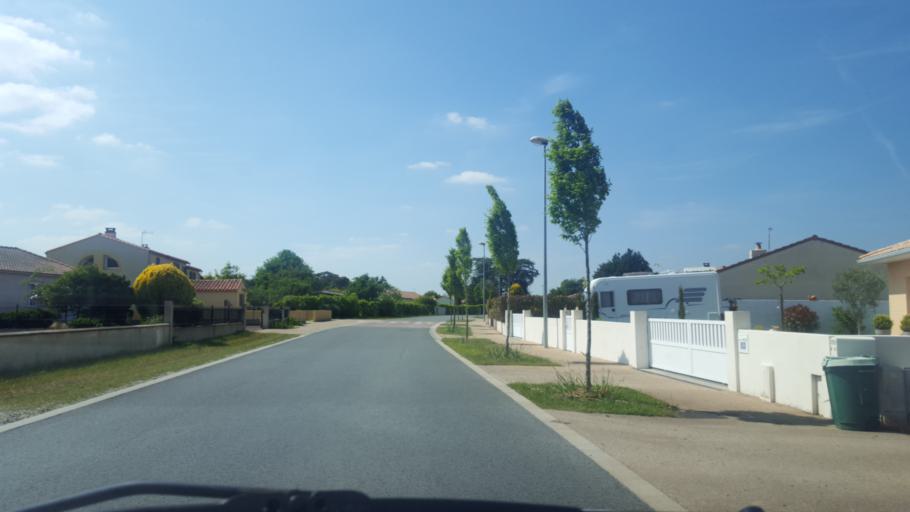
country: FR
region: Pays de la Loire
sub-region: Departement de la Loire-Atlantique
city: La Limouziniere
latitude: 46.9596
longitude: -1.5707
